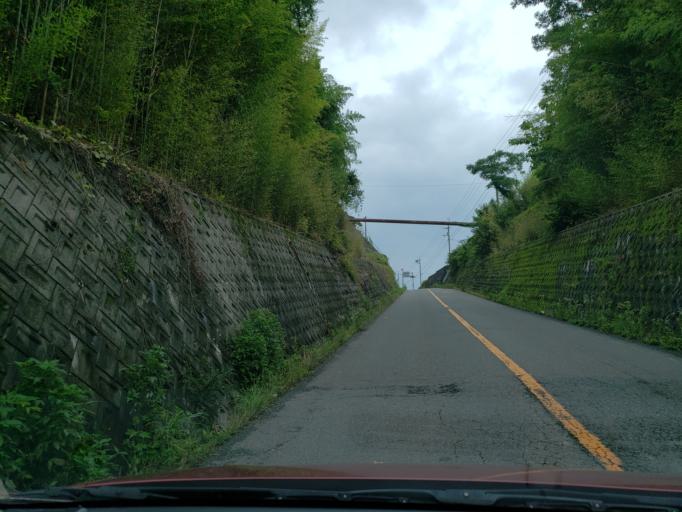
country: JP
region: Tokushima
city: Wakimachi
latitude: 34.1012
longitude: 134.2262
